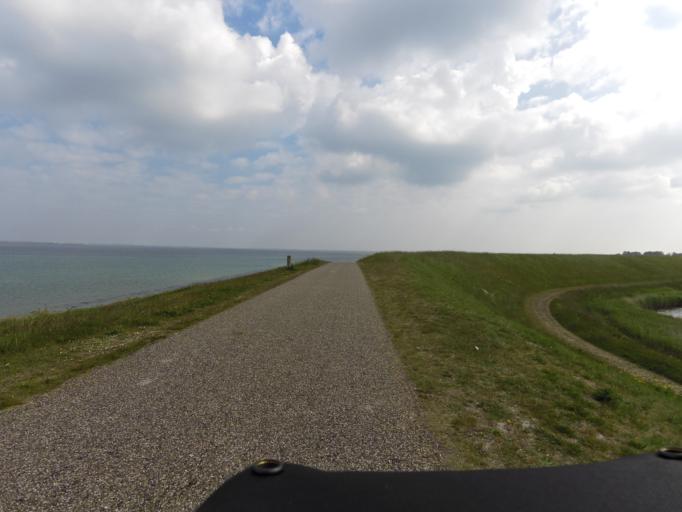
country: NL
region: Zeeland
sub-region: Gemeente Noord-Beveland
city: Kamperland
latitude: 51.5943
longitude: 3.7360
